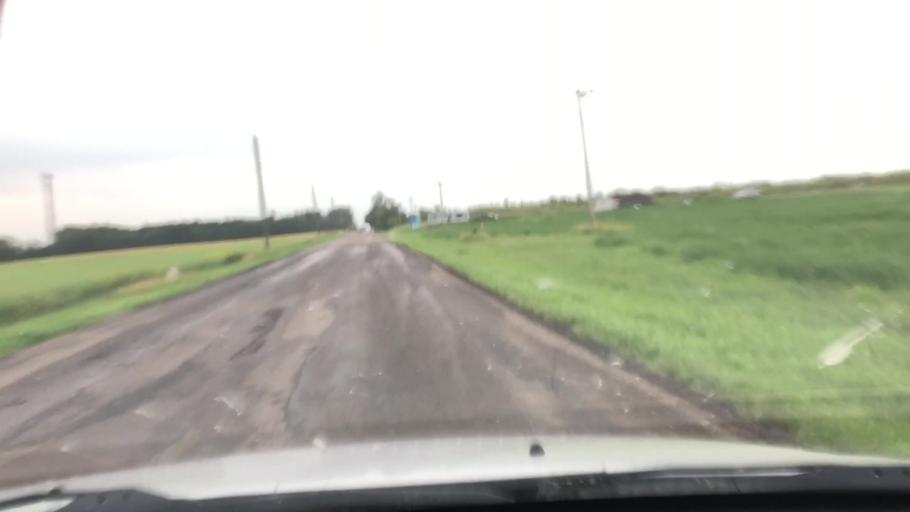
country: CA
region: Alberta
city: Devon
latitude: 53.4233
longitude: -113.6892
